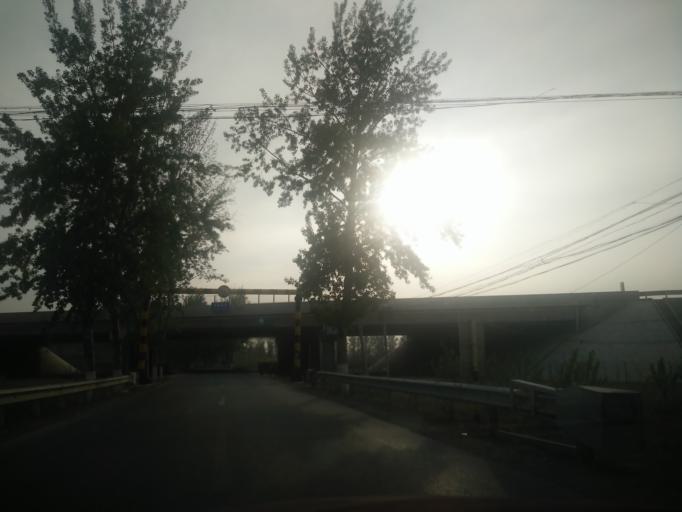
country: CN
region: Beijing
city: Weishanzhuang
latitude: 39.6750
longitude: 116.4499
